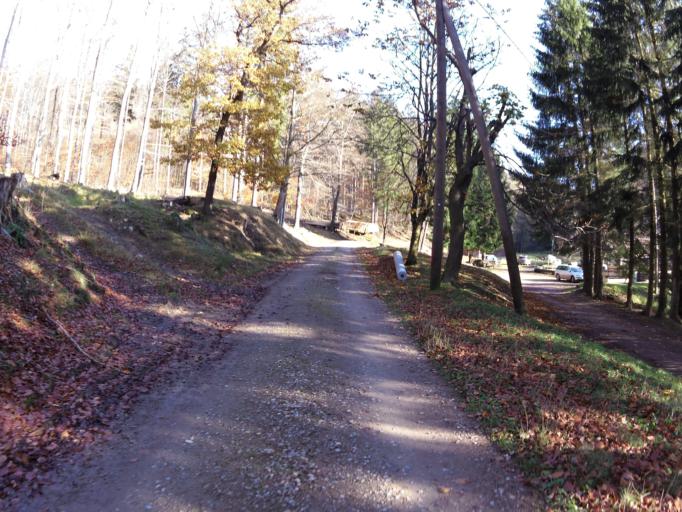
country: DE
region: Thuringia
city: Ruhla
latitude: 50.8828
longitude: 10.3987
